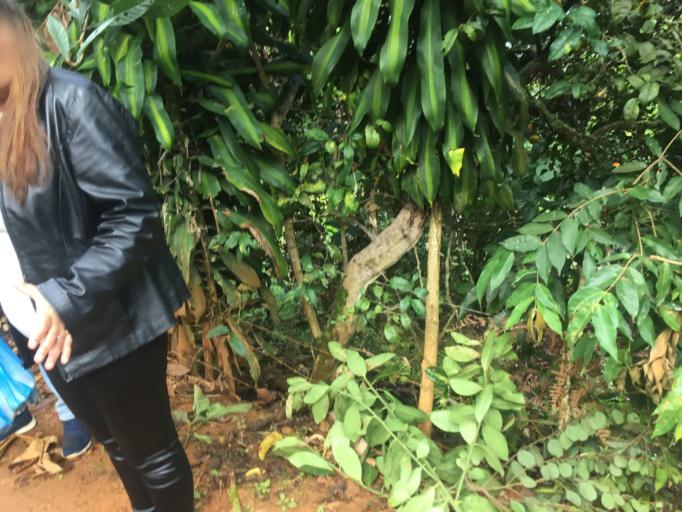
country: CO
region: Valle del Cauca
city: Cali
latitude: 3.4621
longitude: -76.6366
